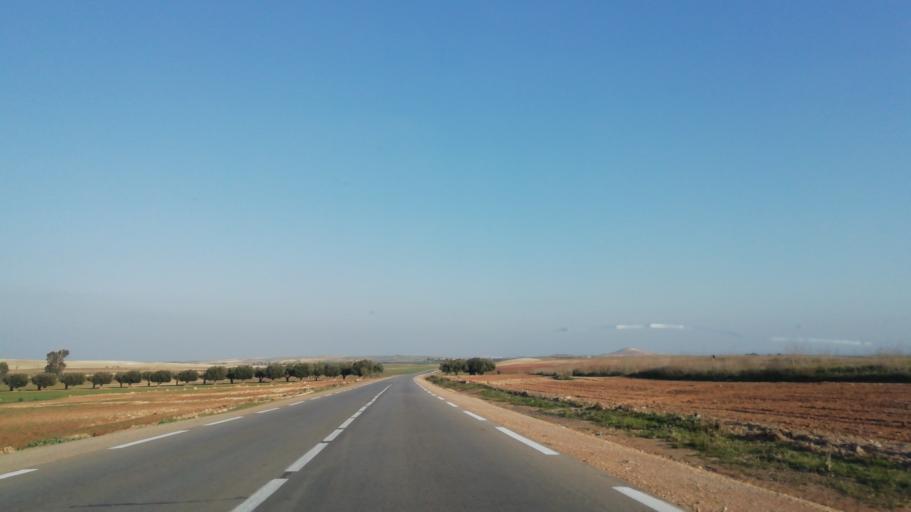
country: DZ
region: Sidi Bel Abbes
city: Sidi Bel Abbes
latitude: 35.1787
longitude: -0.8051
